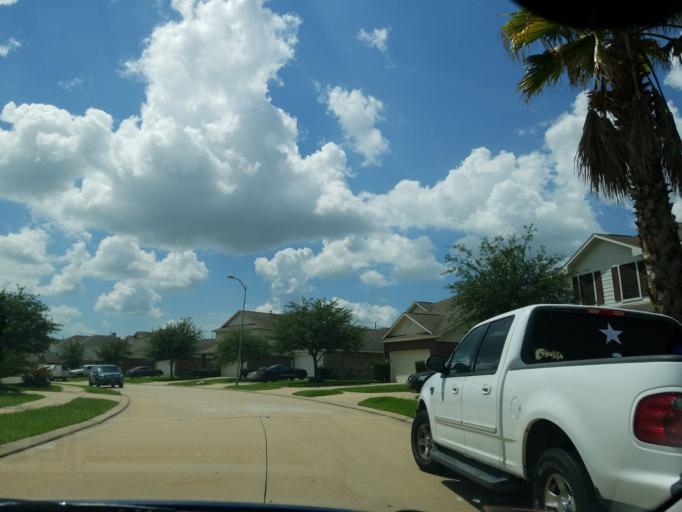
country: US
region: Texas
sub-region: Harris County
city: Cypress
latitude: 29.8779
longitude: -95.7256
